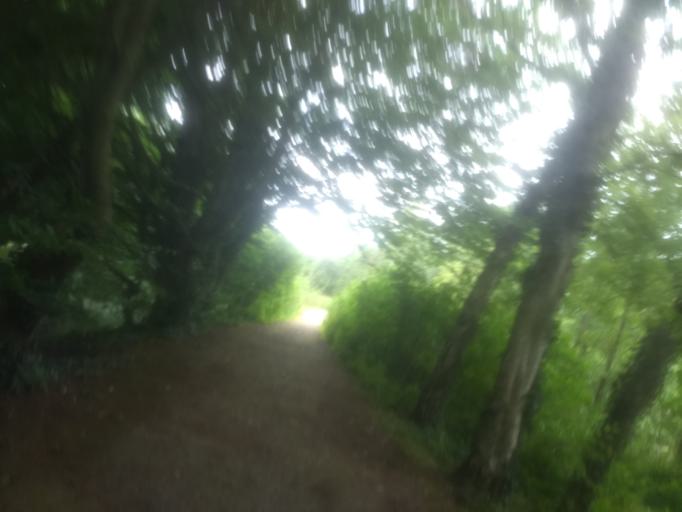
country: FR
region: Nord-Pas-de-Calais
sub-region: Departement du Pas-de-Calais
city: Sainte-Catherine
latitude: 50.3014
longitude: 2.7568
